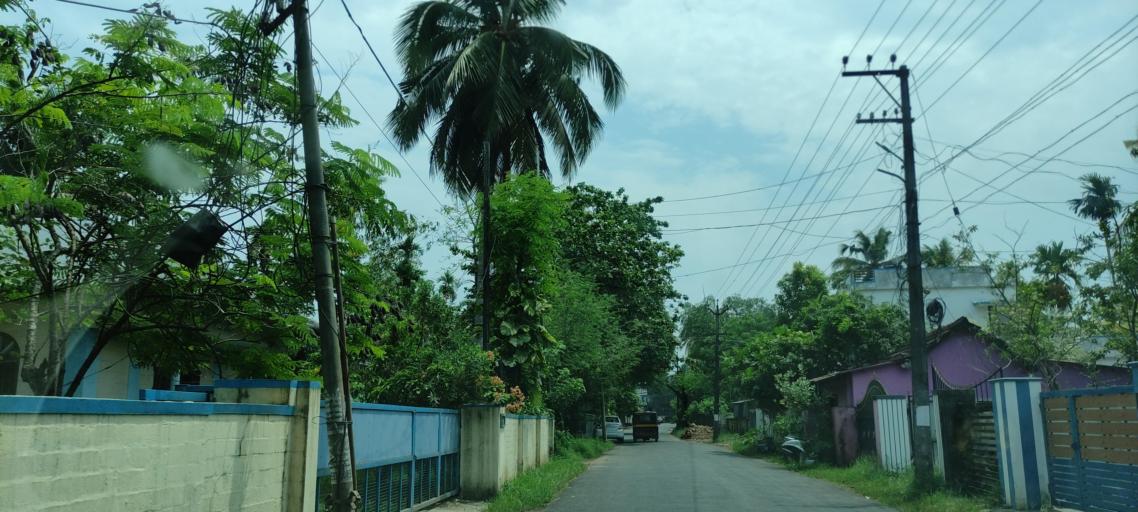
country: IN
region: Kerala
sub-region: Alappuzha
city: Vayalar
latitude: 9.6955
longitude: 76.3375
